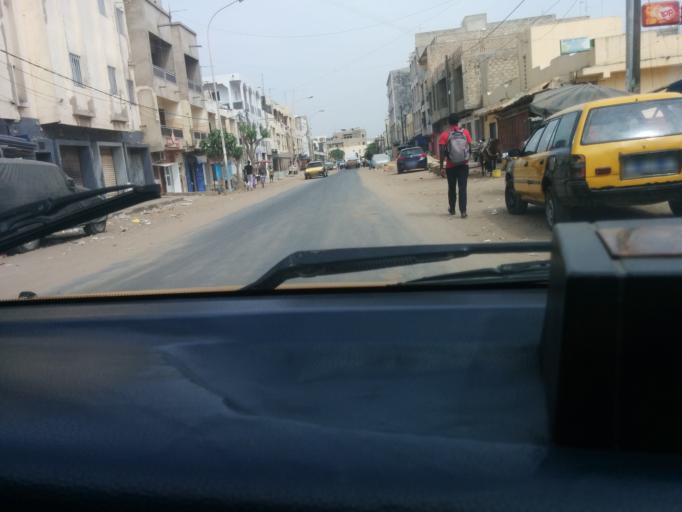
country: SN
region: Dakar
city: Pikine
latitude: 14.7596
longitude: -17.4354
